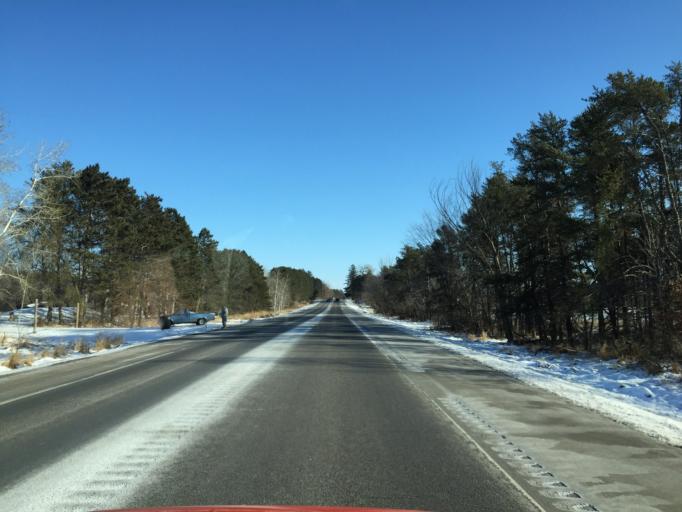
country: US
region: Minnesota
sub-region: Isanti County
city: Cambridge
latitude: 45.5546
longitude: -93.1153
